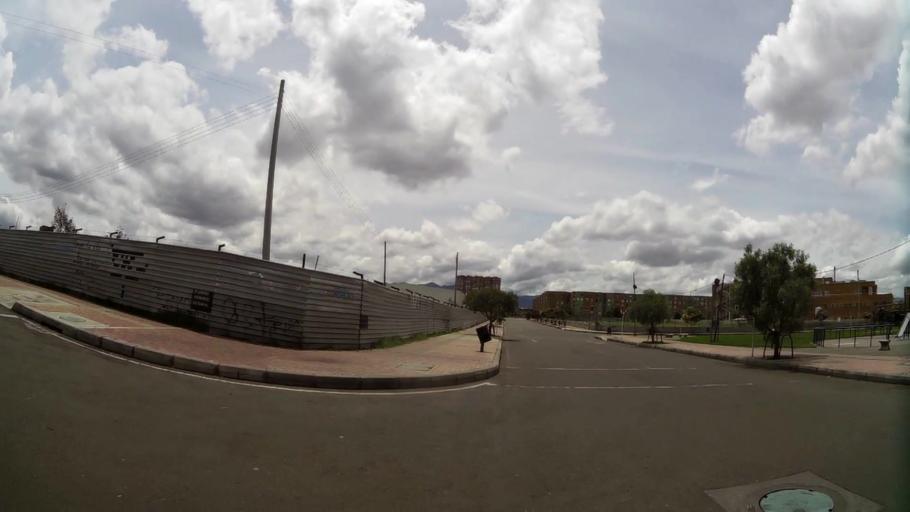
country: CO
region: Bogota D.C.
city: Bogota
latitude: 4.6530
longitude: -74.1489
